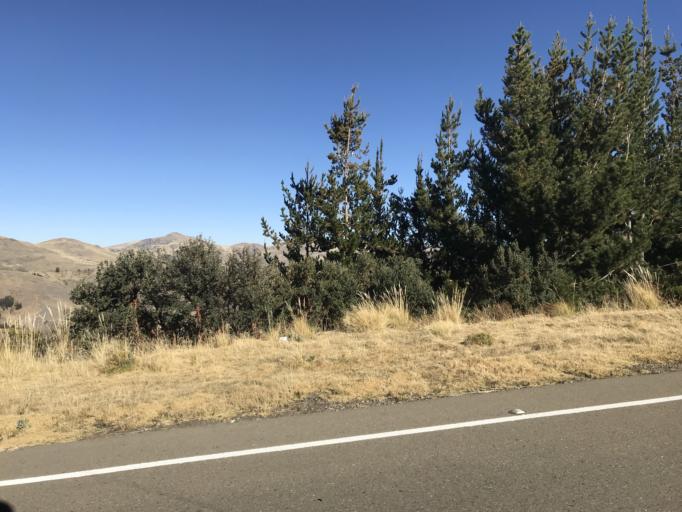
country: PE
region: Puno
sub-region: Yunguyo
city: Yunguyo
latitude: -16.1815
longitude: -68.9818
